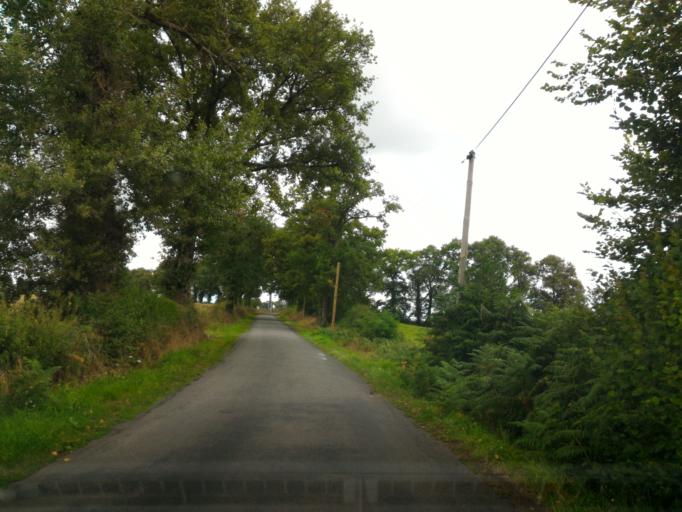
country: FR
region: Poitou-Charentes
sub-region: Departement de la Charente
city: Chabanais
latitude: 45.8854
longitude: 0.7411
